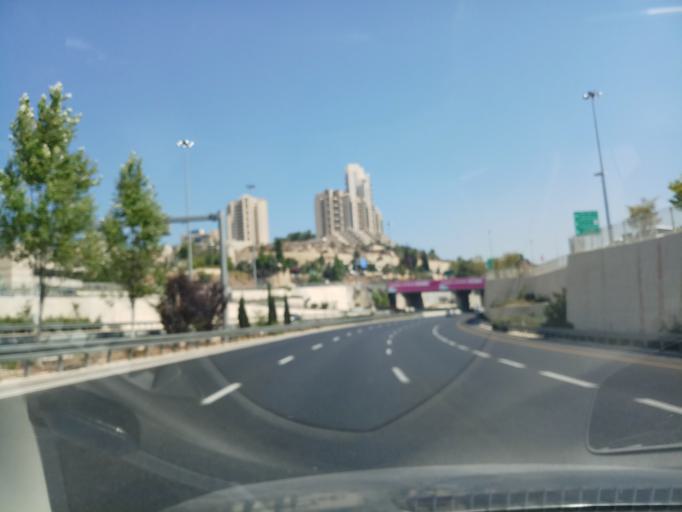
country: PS
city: Khallat Hamamah
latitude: 31.7510
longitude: 35.1890
